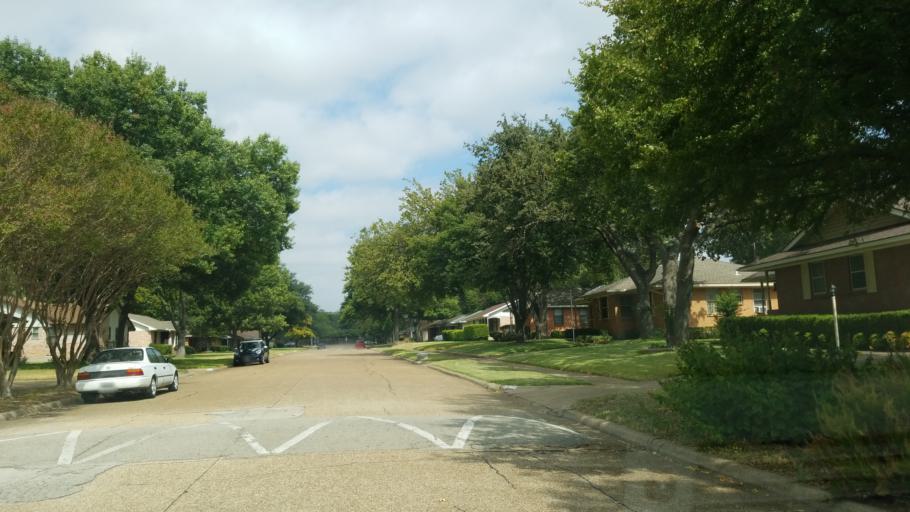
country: US
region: Texas
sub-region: Dallas County
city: Garland
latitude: 32.8921
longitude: -96.6597
